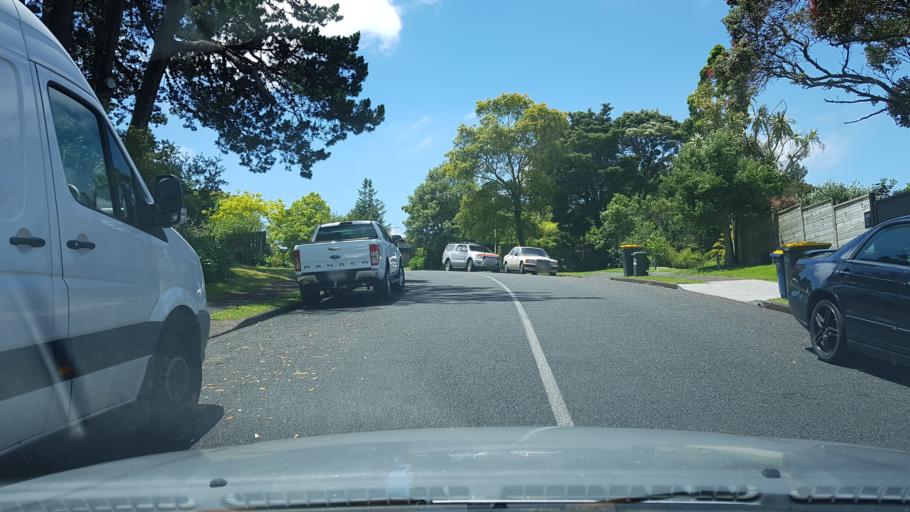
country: NZ
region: Auckland
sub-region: Auckland
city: North Shore
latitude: -36.8024
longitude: 174.7197
